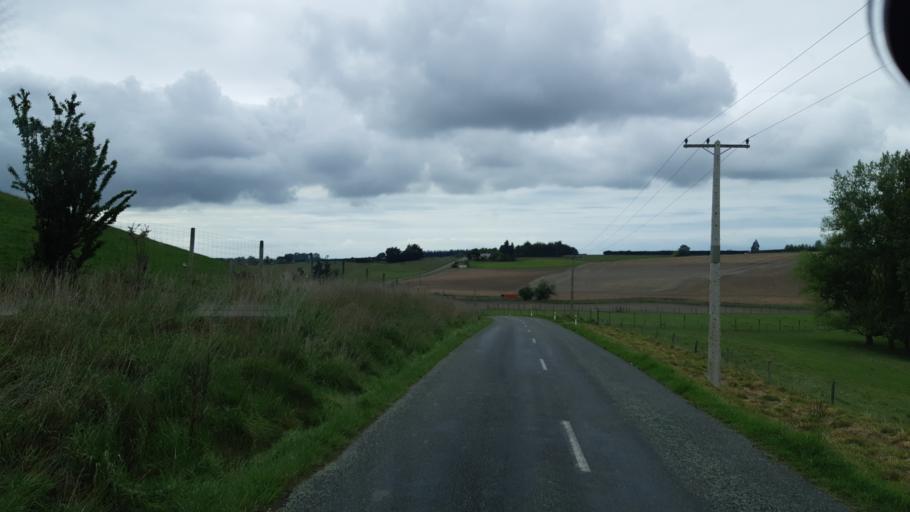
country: NZ
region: Canterbury
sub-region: Timaru District
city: Pleasant Point
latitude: -44.3282
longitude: 171.1477
